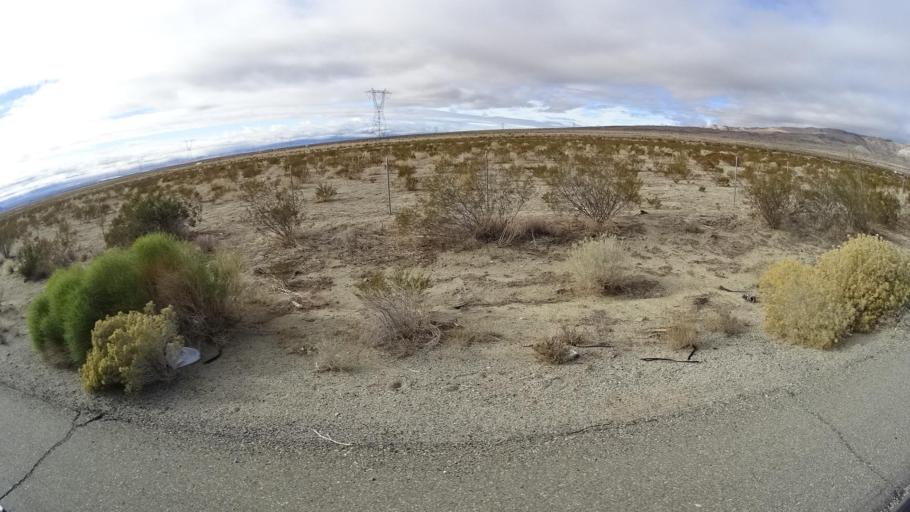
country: US
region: California
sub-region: Kern County
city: Mojave
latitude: 34.9792
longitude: -118.3127
